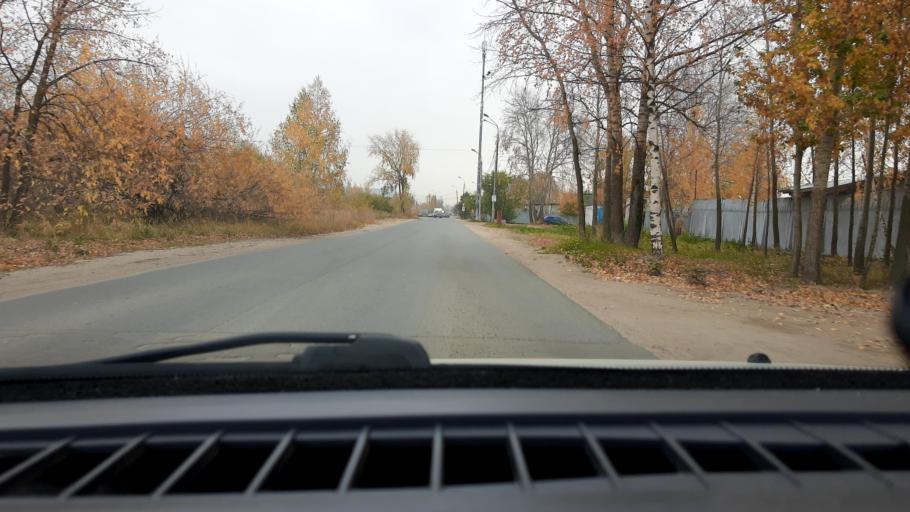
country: RU
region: Nizjnij Novgorod
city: Gorbatovka
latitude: 56.3527
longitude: 43.7979
